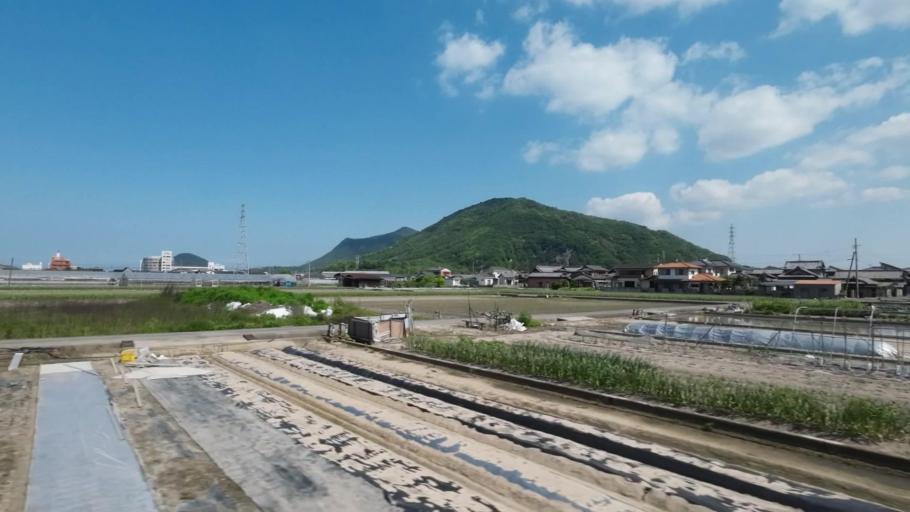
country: JP
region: Kagawa
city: Kan'onjicho
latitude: 34.1297
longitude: 133.6729
